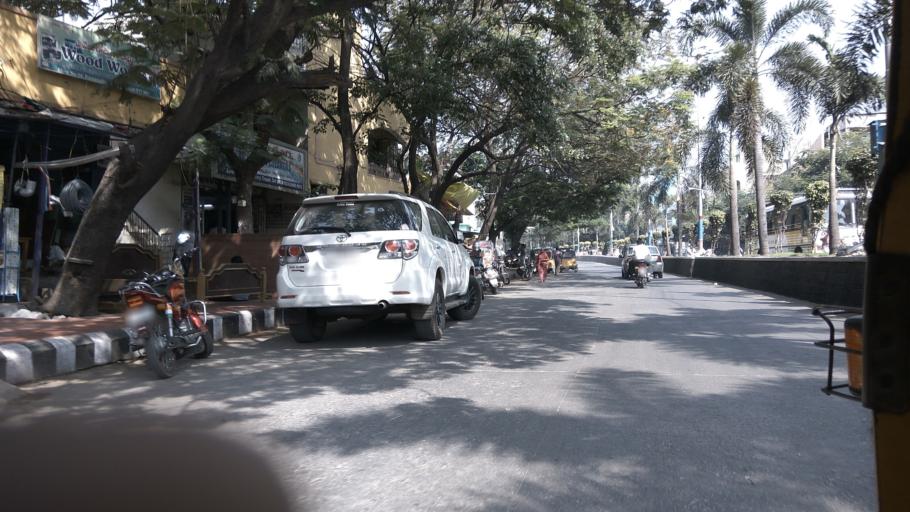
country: IN
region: Andhra Pradesh
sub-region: Chittoor
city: Tirupati
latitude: 13.6346
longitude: 79.4131
